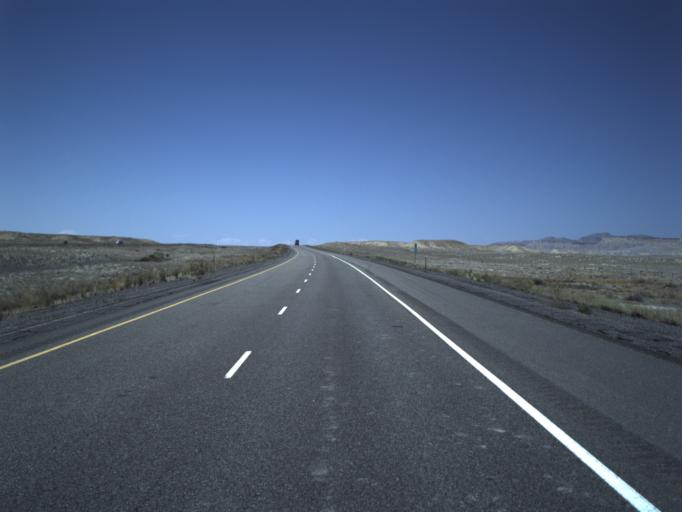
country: US
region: Utah
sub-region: Grand County
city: Moab
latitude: 38.9426
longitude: -109.5289
